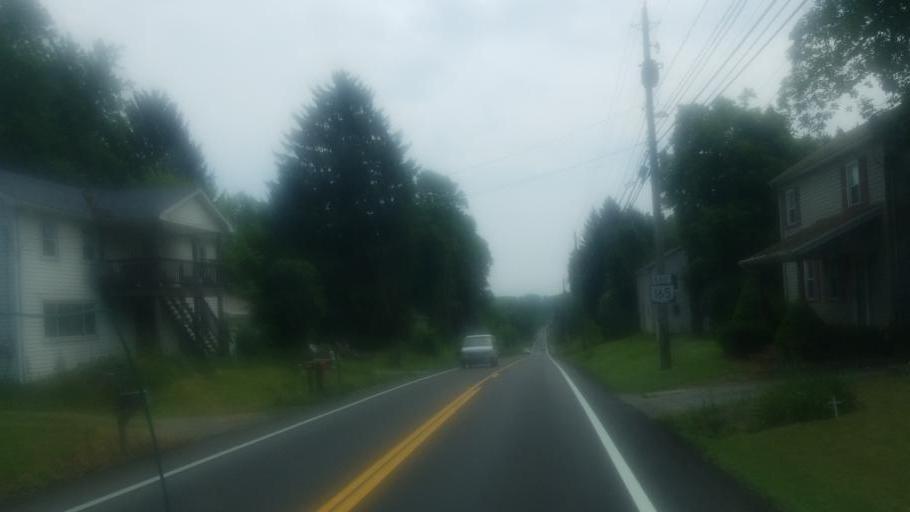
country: US
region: Ohio
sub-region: Columbiana County
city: Columbiana
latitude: 40.9441
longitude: -80.6972
